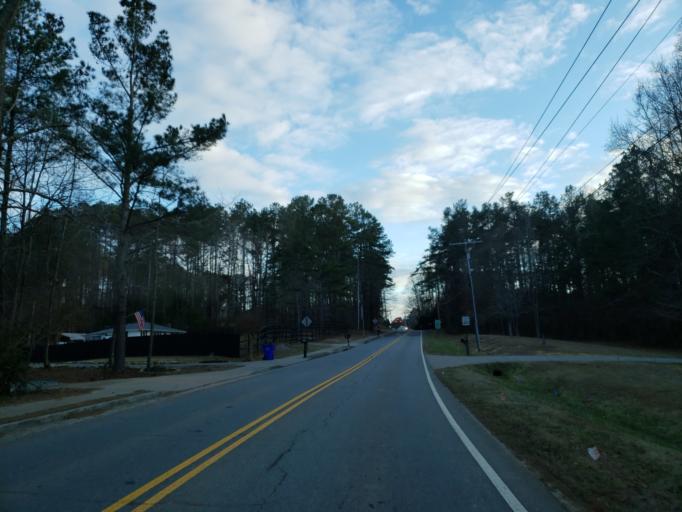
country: US
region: Georgia
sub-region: Cobb County
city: Kennesaw
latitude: 34.0017
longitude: -84.6761
